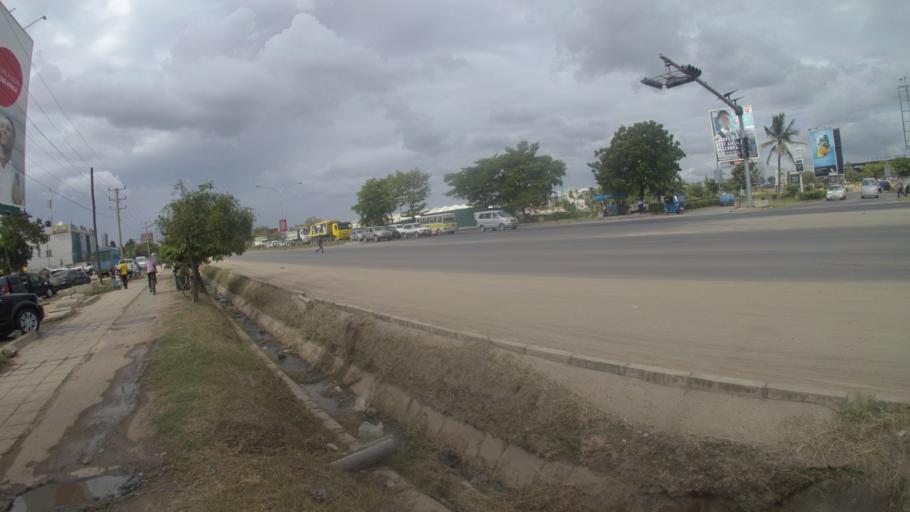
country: TZ
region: Dar es Salaam
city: Dar es Salaam
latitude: -6.8630
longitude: 39.2061
